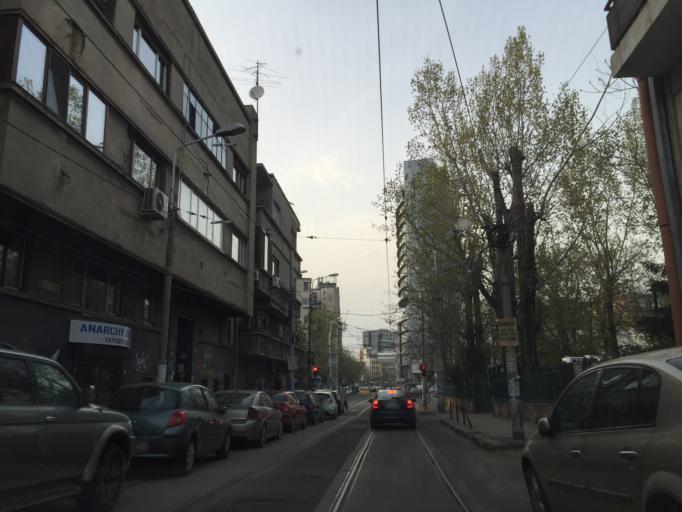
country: RO
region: Bucuresti
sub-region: Municipiul Bucuresti
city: Bucharest
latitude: 44.4357
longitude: 26.1110
